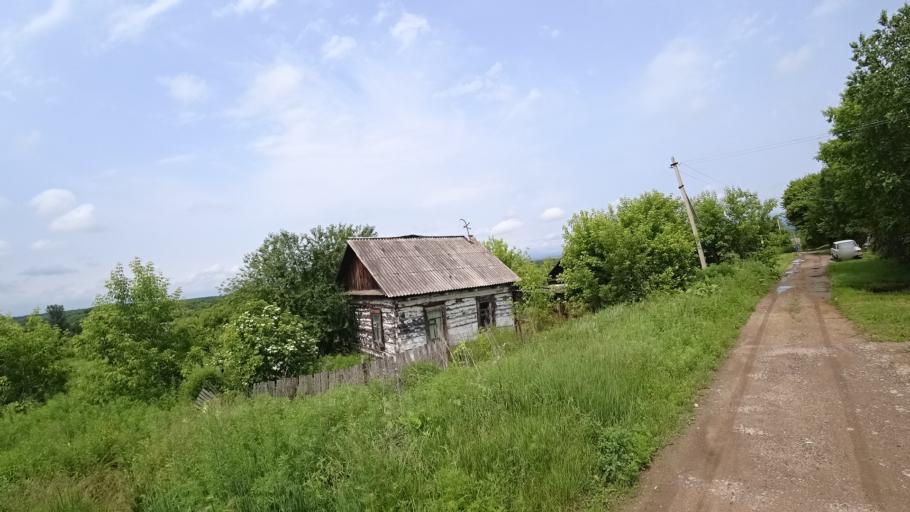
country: RU
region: Primorskiy
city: Novosysoyevka
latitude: 44.2528
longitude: 133.3781
